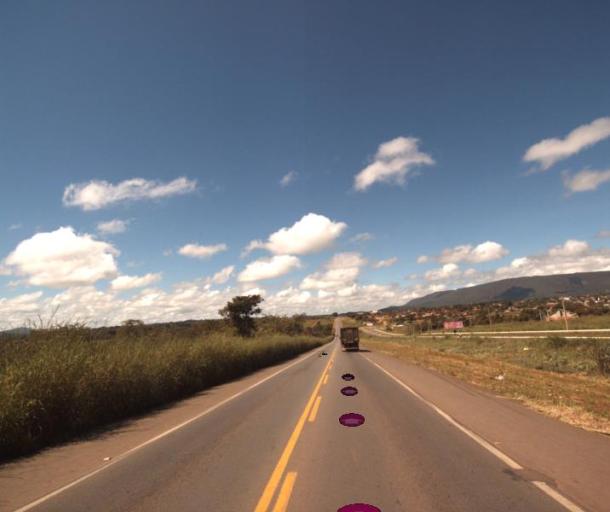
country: BR
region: Goias
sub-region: Jaragua
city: Jaragua
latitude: -15.7432
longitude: -49.3199
